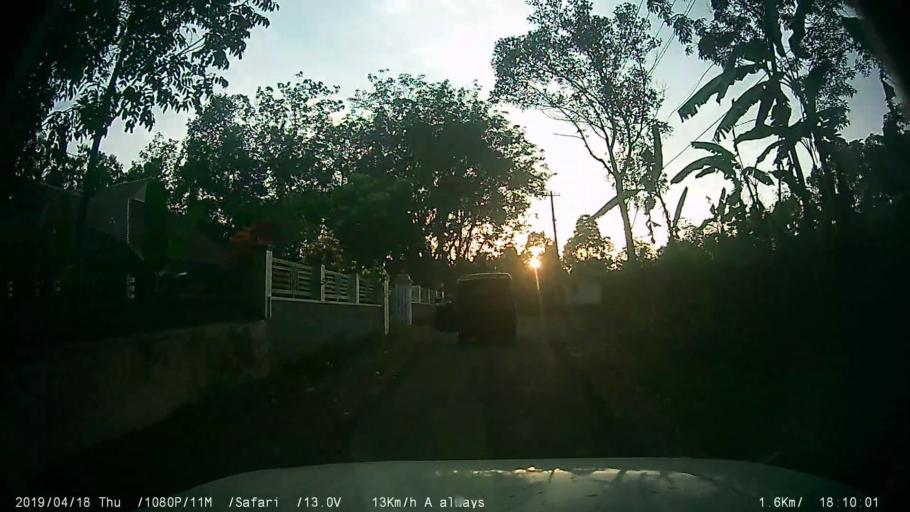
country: IN
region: Kerala
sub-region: Kottayam
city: Palackattumala
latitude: 9.7781
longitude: 76.5794
